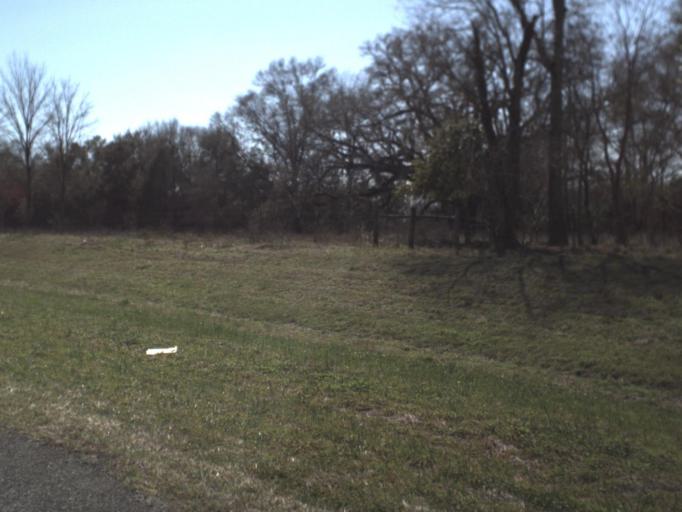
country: US
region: Florida
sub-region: Jackson County
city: Graceville
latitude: 30.8975
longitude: -85.3724
